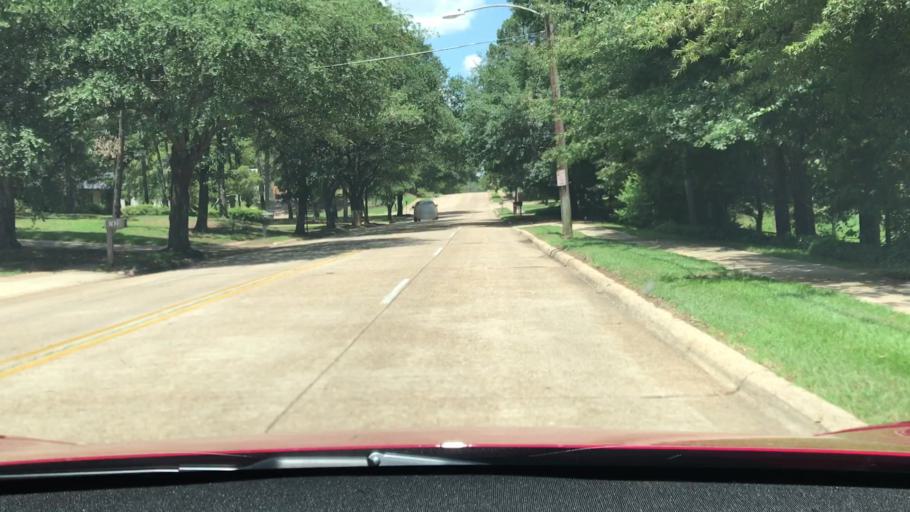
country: US
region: Louisiana
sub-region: Bossier Parish
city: Bossier City
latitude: 32.4369
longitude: -93.7332
